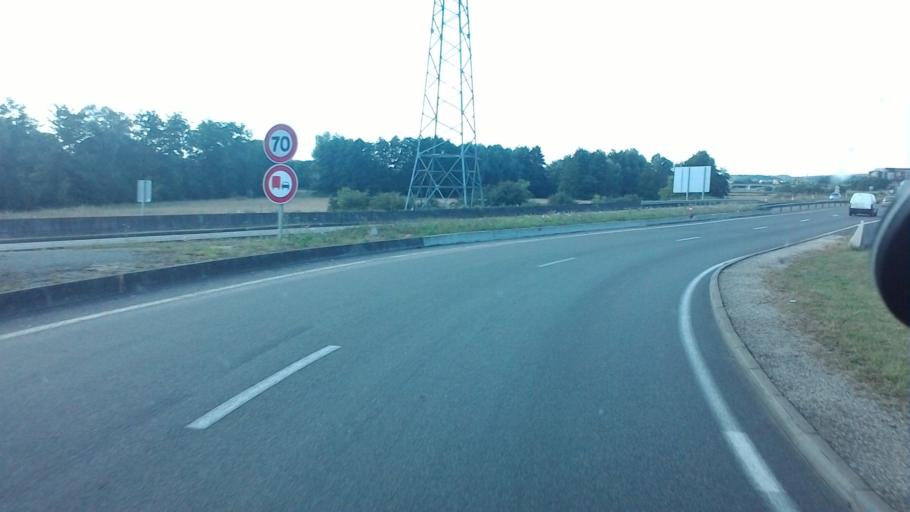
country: FR
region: Franche-Comte
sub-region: Departement de la Haute-Saone
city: Noidans-les-Vesoul
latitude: 47.6269
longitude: 6.1383
